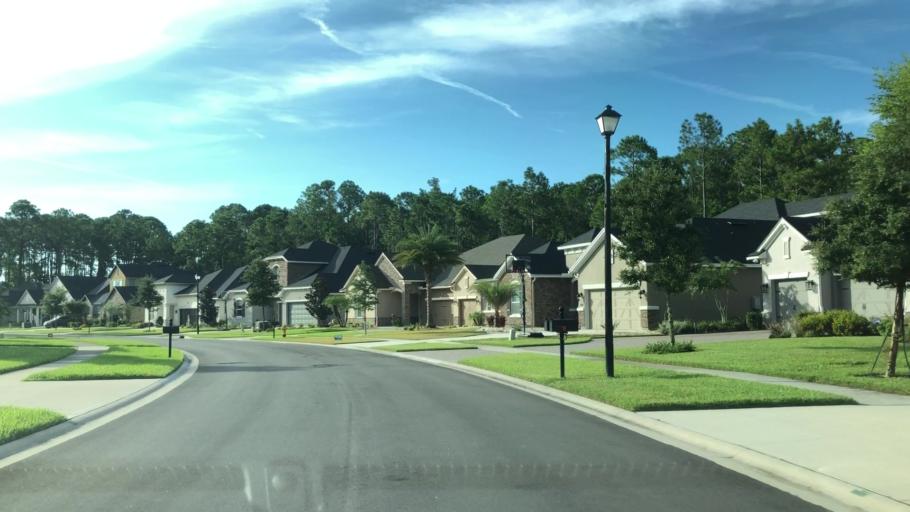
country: US
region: Florida
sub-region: Saint Johns County
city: Palm Valley
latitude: 30.1312
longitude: -81.4273
